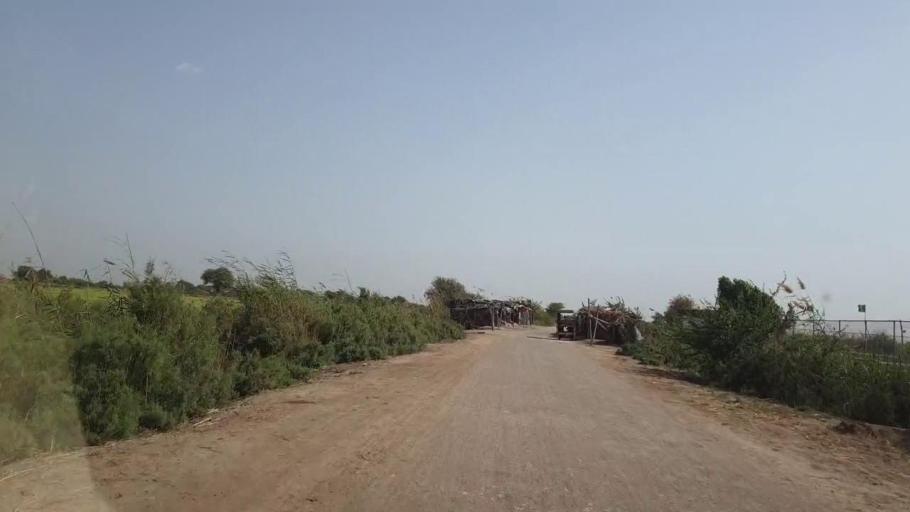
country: PK
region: Sindh
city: Rajo Khanani
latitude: 25.0510
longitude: 68.8420
